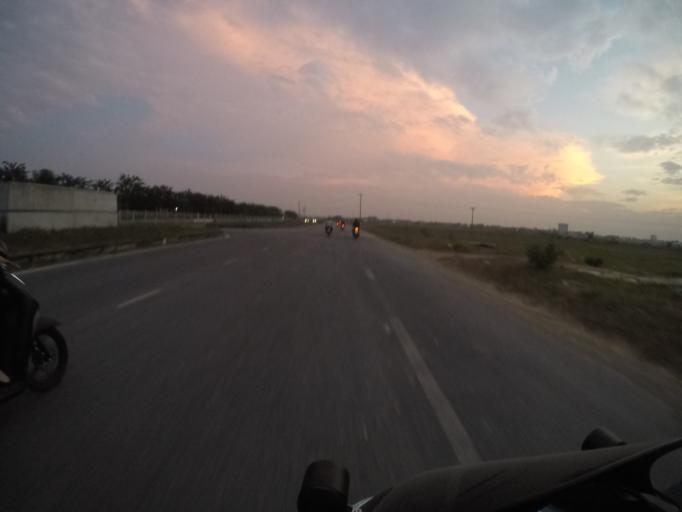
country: VN
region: Vinh Phuc
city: Phuc Yen
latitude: 21.2488
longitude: 105.7216
